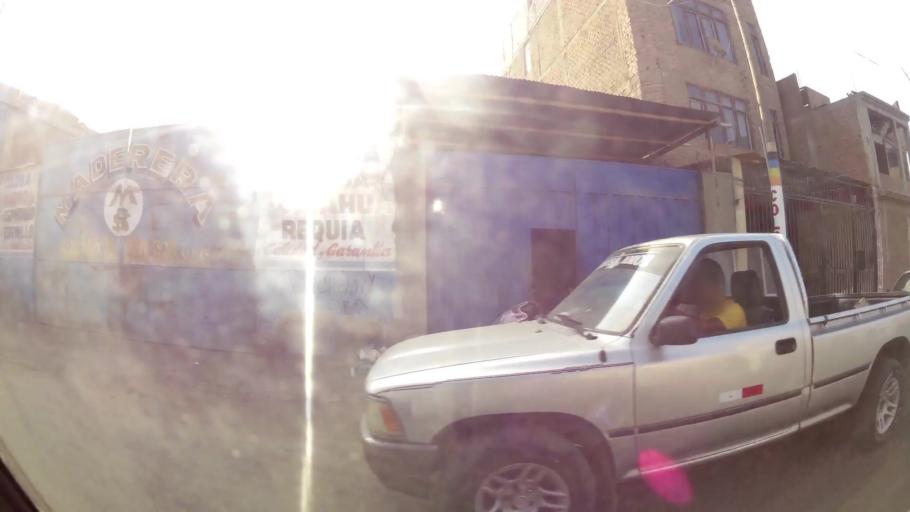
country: PE
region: La Libertad
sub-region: Provincia de Trujillo
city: El Porvenir
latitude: -8.0868
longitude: -79.0113
